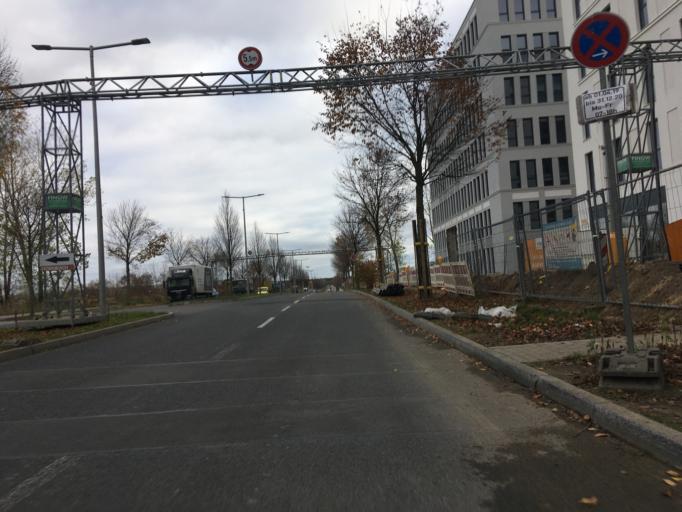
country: DE
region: Berlin
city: Altglienicke
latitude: 52.3962
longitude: 13.5406
